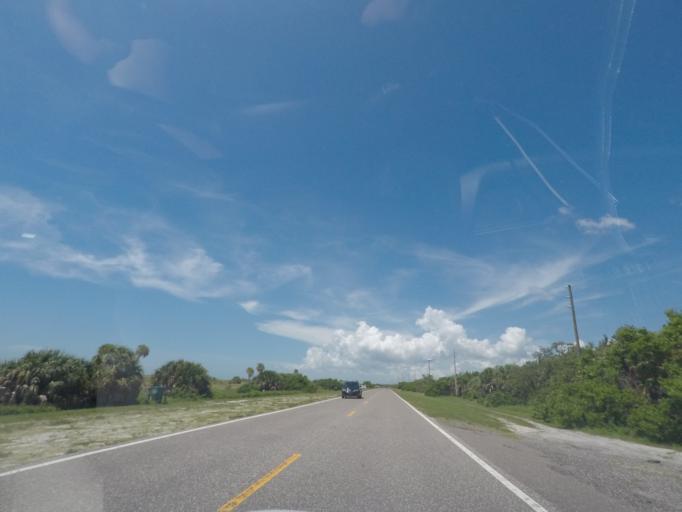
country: US
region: Florida
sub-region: Pinellas County
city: Tierra Verde
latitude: 27.6204
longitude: -82.7349
